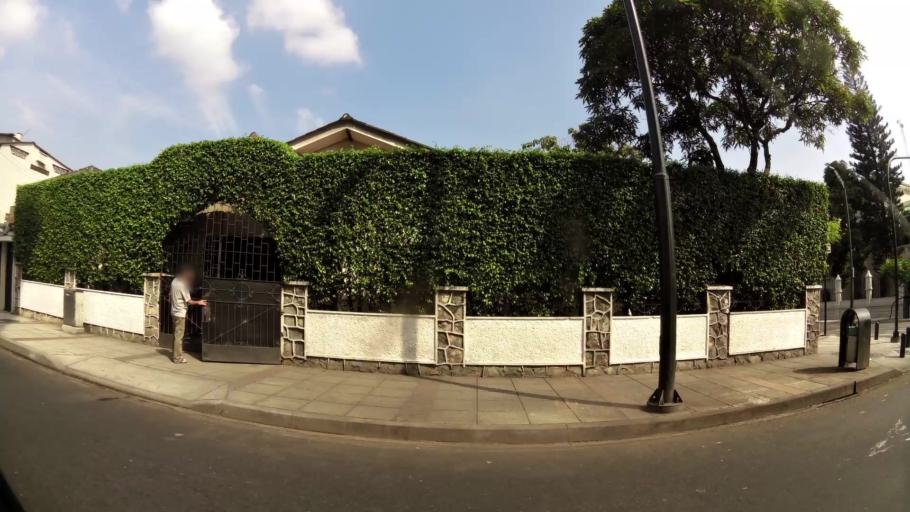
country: EC
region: Guayas
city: Guayaquil
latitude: -2.1893
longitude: -79.8969
